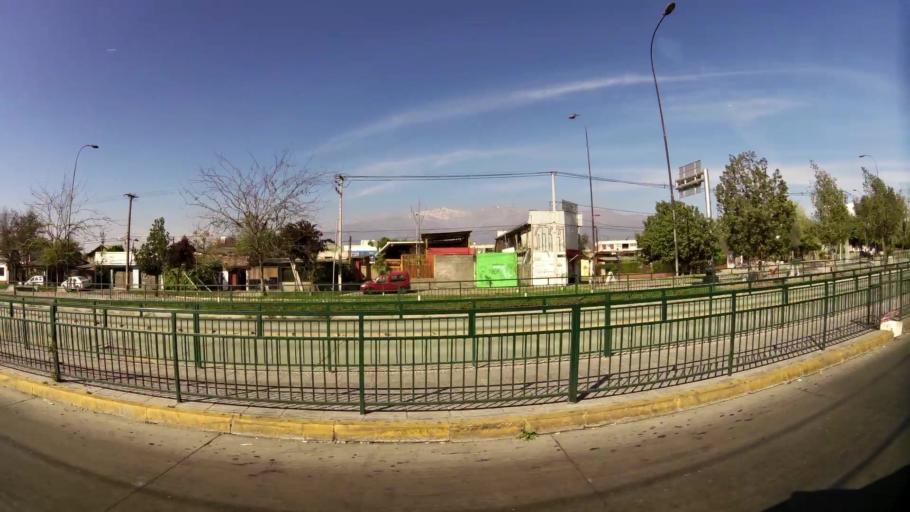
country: CL
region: Santiago Metropolitan
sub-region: Provincia de Santiago
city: Santiago
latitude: -33.5069
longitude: -70.6264
